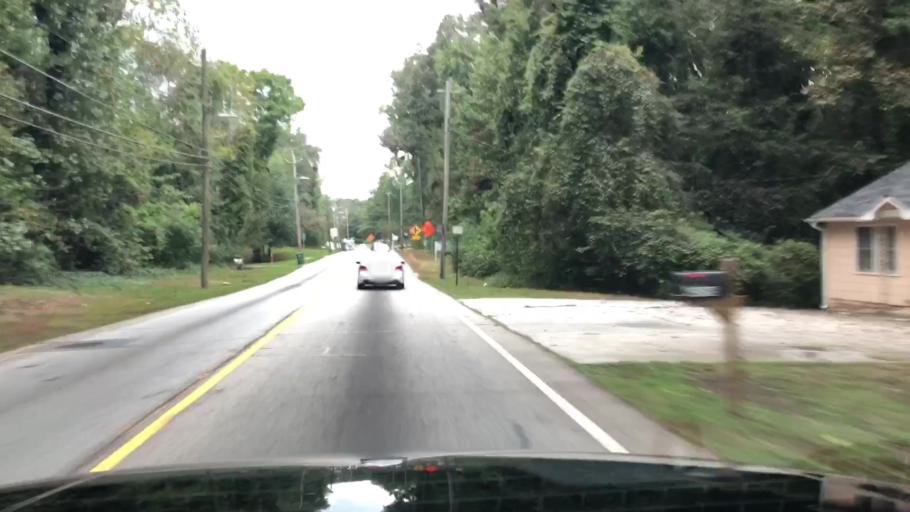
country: US
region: Georgia
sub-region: Fulton County
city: College Park
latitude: 33.6946
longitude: -84.5221
